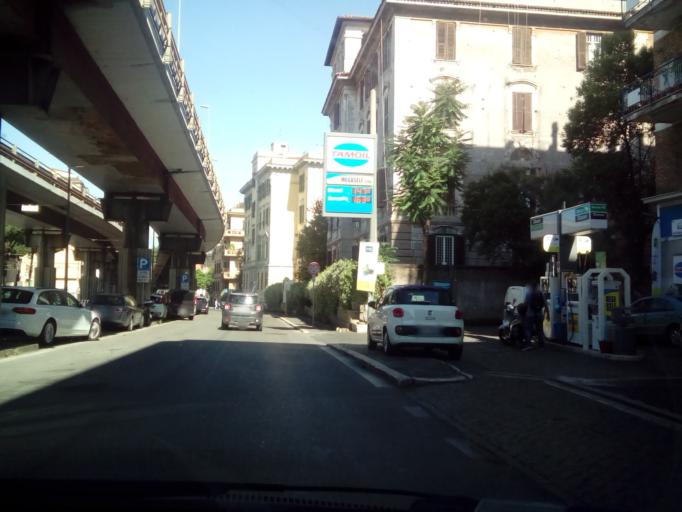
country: IT
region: Latium
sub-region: Citta metropolitana di Roma Capitale
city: Rome
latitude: 41.8910
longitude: 12.5235
